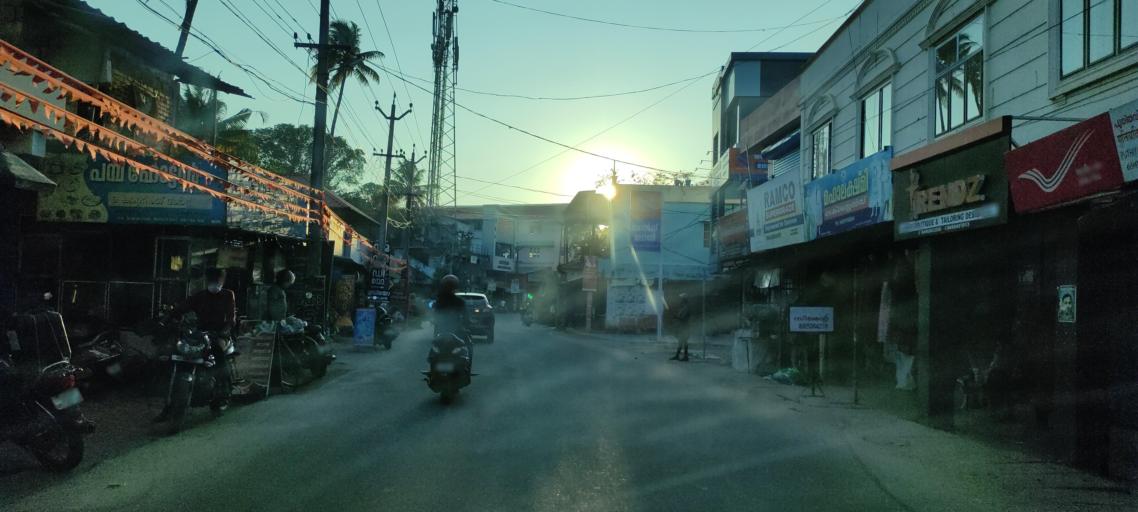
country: IN
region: Kerala
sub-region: Alappuzha
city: Kayankulam
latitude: 9.1898
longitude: 76.4698
